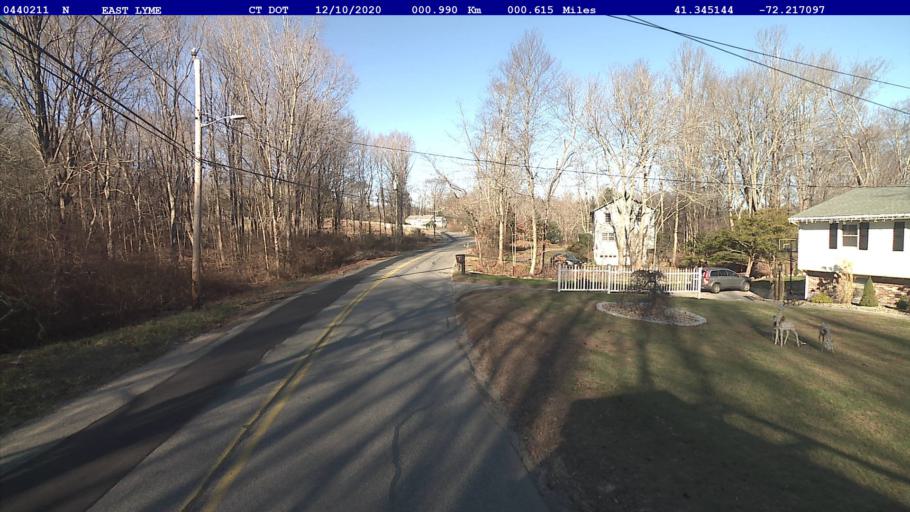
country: US
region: Connecticut
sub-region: New London County
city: Niantic
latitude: 41.3452
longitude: -72.2171
